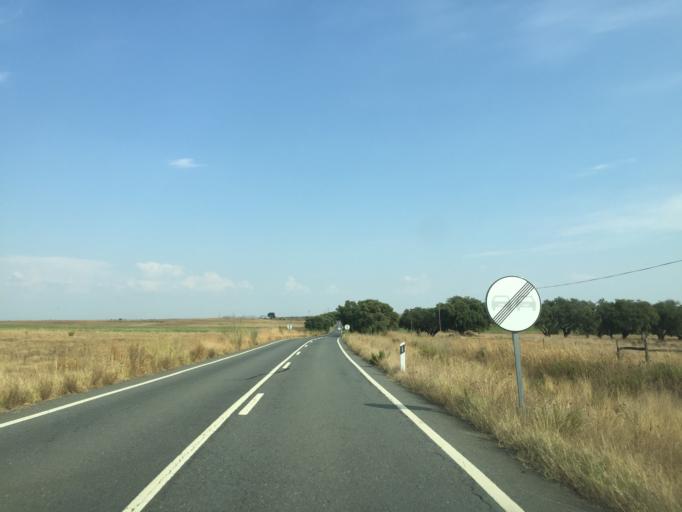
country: PT
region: Beja
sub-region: Aljustrel
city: Aljustrel
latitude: 37.9337
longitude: -8.3525
